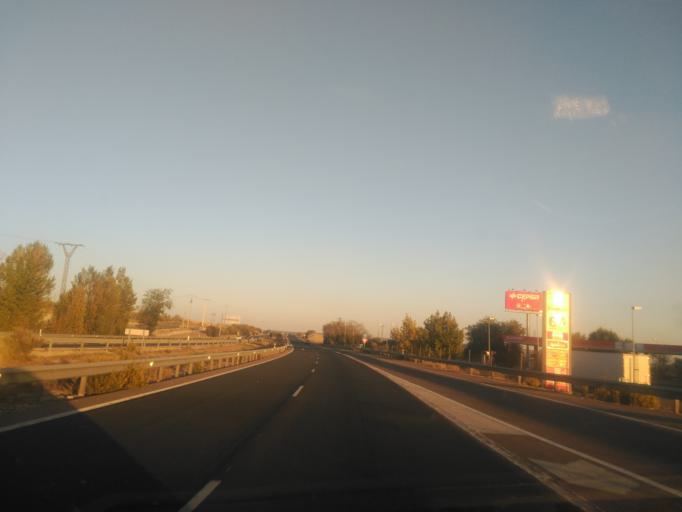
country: ES
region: Castille and Leon
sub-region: Provincia de Valladolid
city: Cisterniga
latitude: 41.5987
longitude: -4.6565
